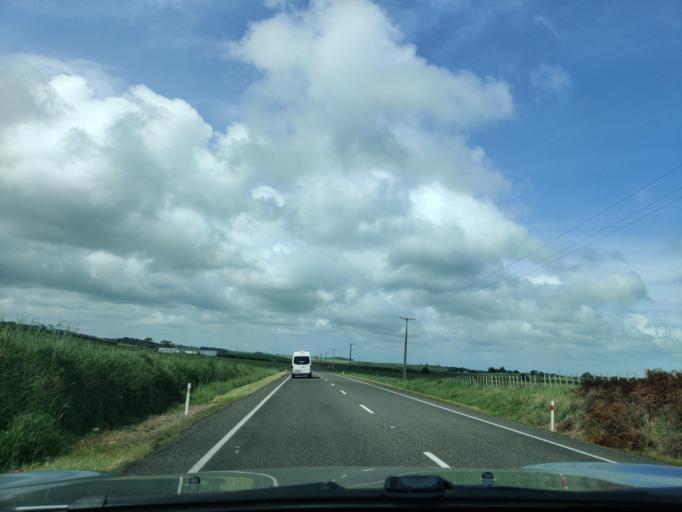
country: NZ
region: Manawatu-Wanganui
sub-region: Wanganui District
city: Wanganui
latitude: -39.8146
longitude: 174.8170
